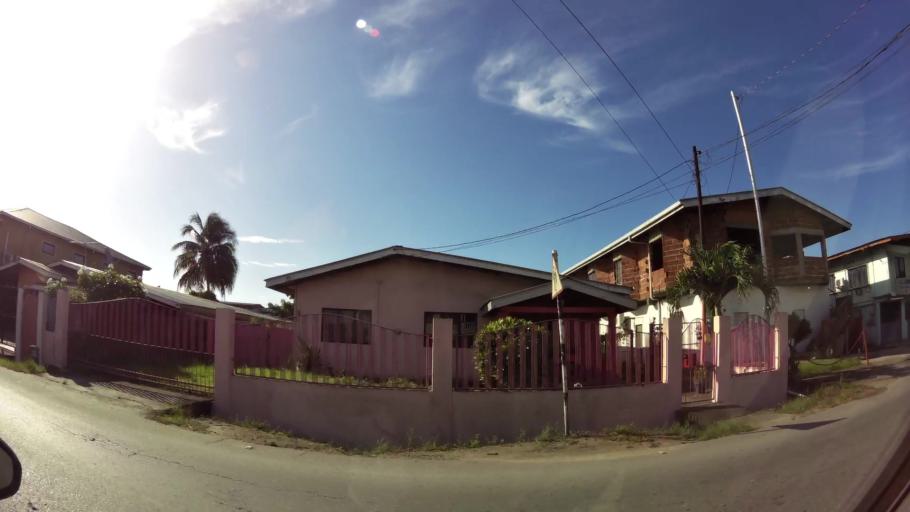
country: TT
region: Chaguanas
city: Chaguanas
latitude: 10.5136
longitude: -61.3795
